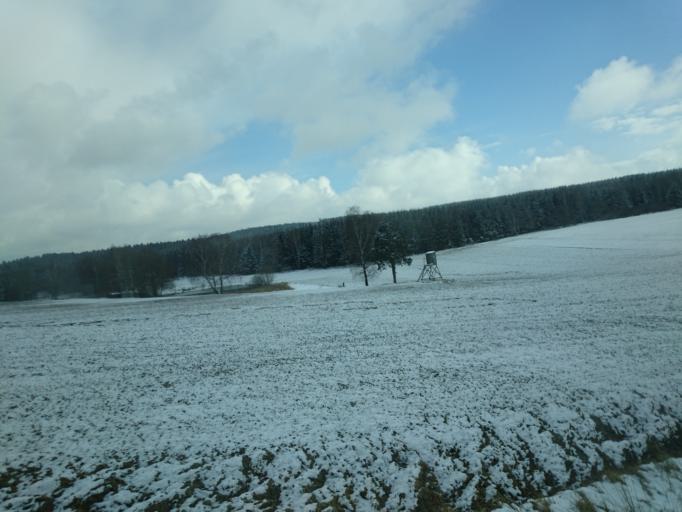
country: DE
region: Thuringia
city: Kospoda
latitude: 50.7031
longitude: 11.7663
